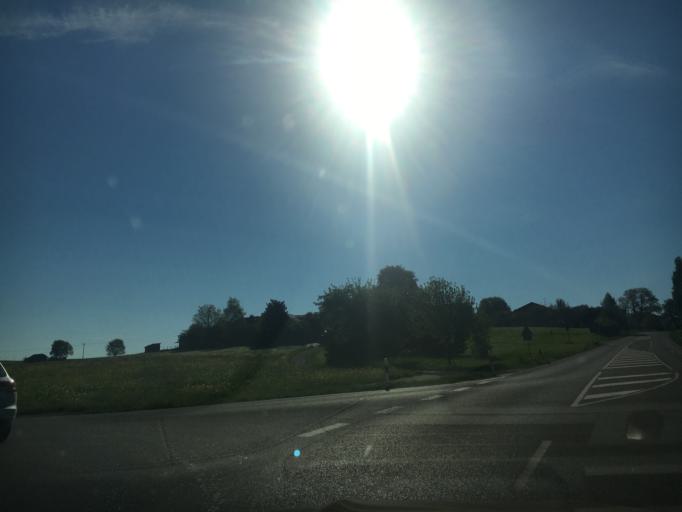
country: DE
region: Bavaria
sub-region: Upper Bavaria
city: Traunreut
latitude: 47.9687
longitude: 12.6122
